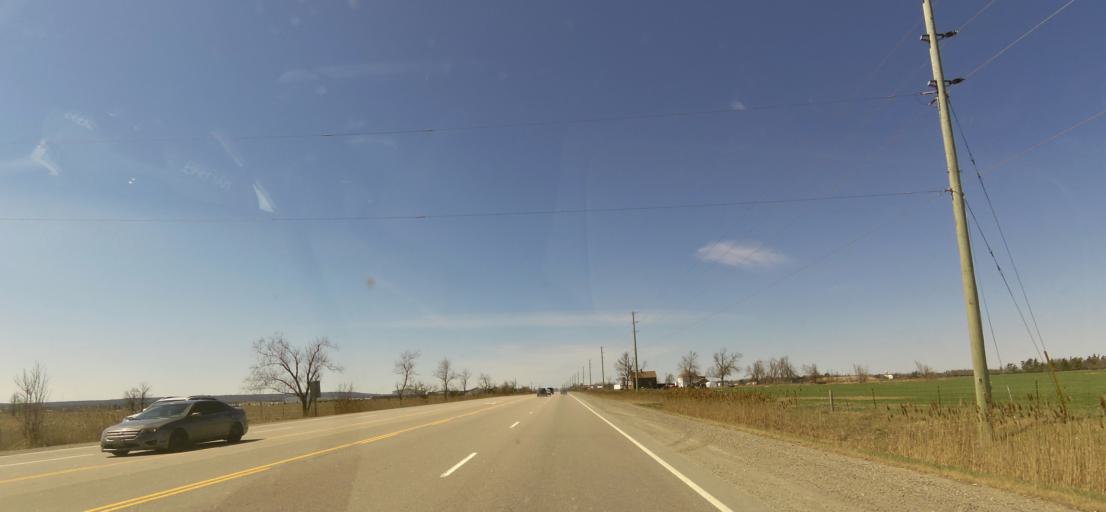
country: CA
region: Ontario
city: Brampton
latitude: 43.7664
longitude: -79.8686
